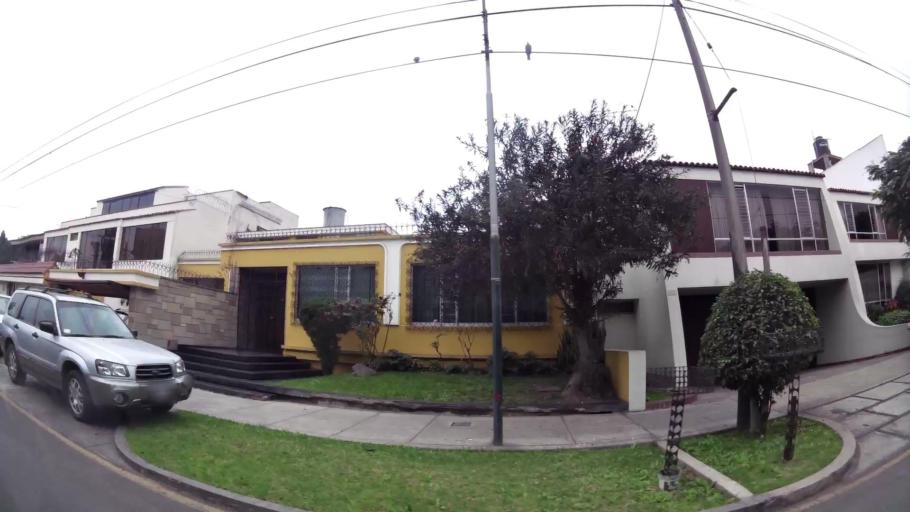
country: PE
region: Lima
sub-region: Lima
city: San Luis
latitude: -12.0951
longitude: -77.0166
